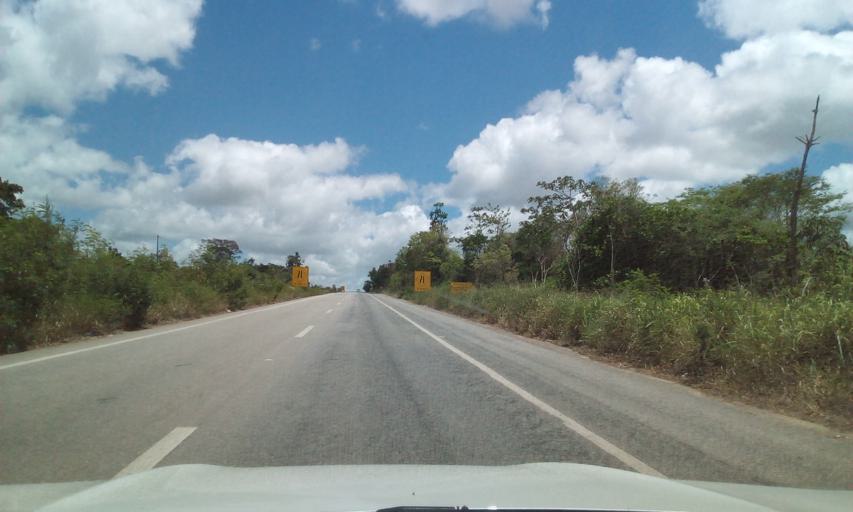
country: BR
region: Alagoas
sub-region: Campo Alegre
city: Campo Alegre
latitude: -9.9074
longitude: -36.3216
